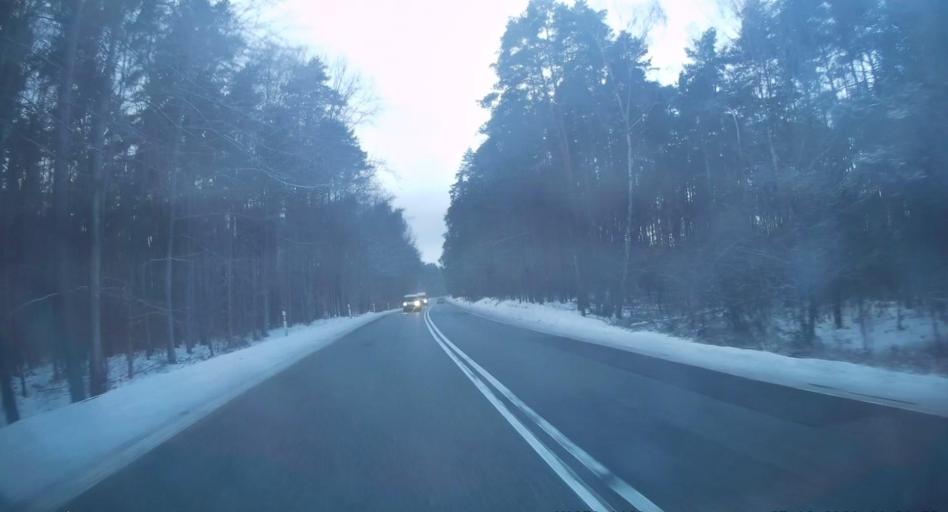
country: PL
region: Swietokrzyskie
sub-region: Powiat konecki
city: Radoszyce
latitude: 51.0981
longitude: 20.3317
